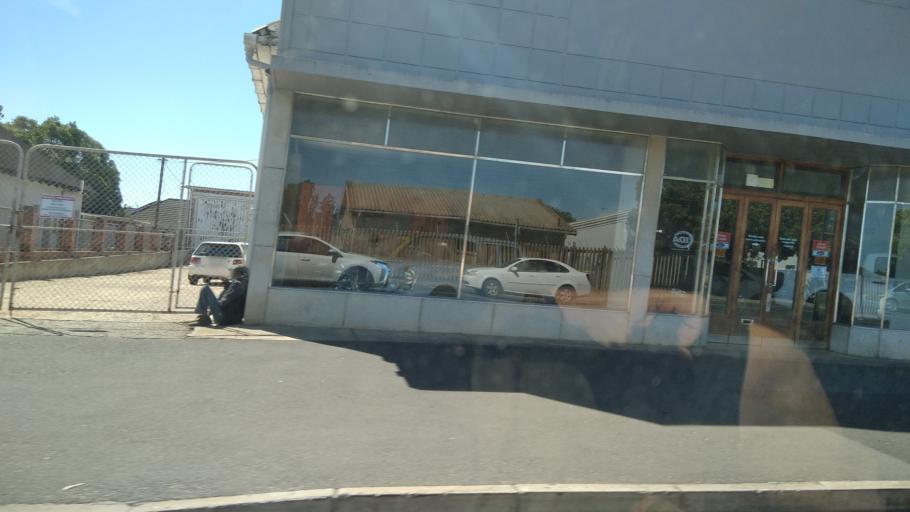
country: ZA
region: Western Cape
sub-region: West Coast District Municipality
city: Moorreesburg
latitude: -33.0631
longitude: 18.3511
